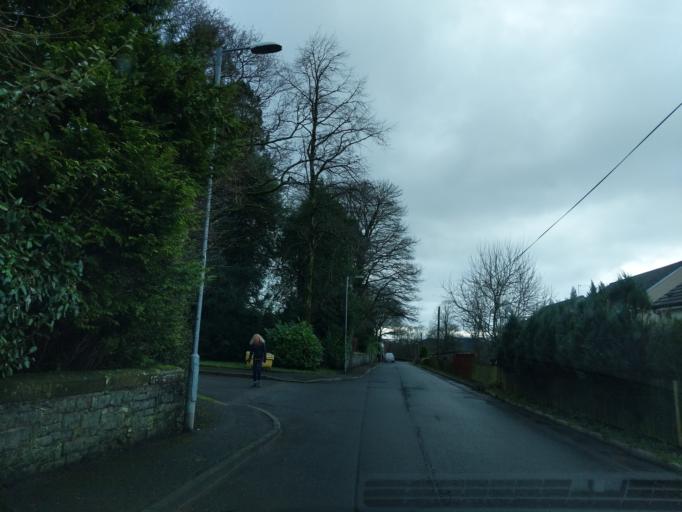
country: GB
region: Scotland
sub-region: Dumfries and Galloway
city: Moffat
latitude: 55.3325
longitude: -3.4330
